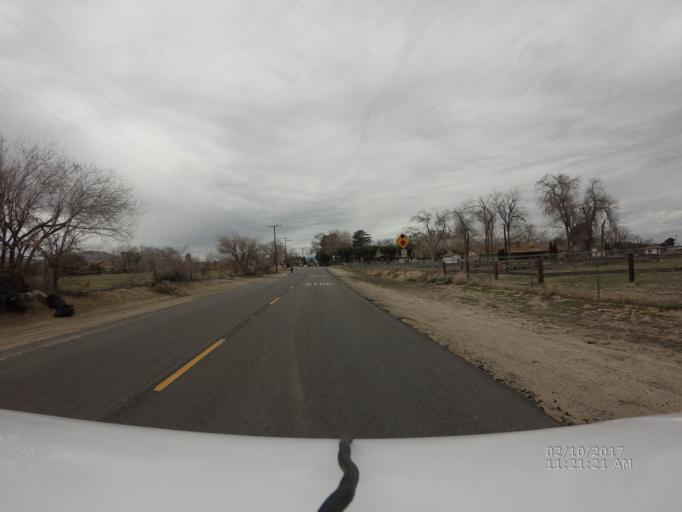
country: US
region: California
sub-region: Los Angeles County
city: Littlerock
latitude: 34.5284
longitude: -117.9826
